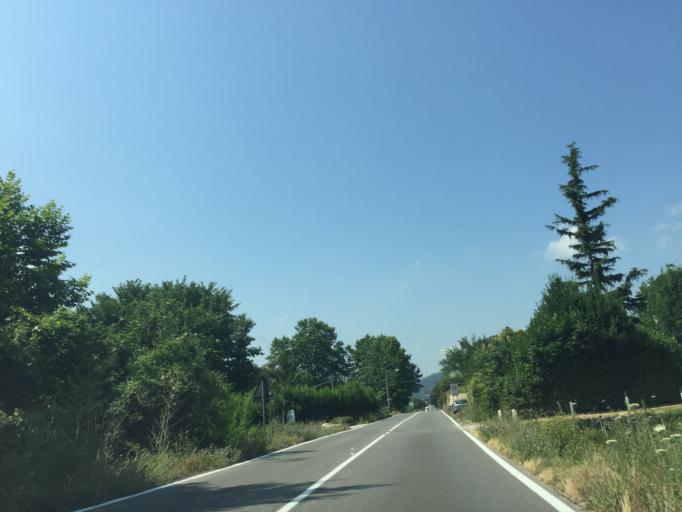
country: IT
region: Tuscany
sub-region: Province of Pisa
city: Asciano
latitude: 43.7979
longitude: 10.4831
